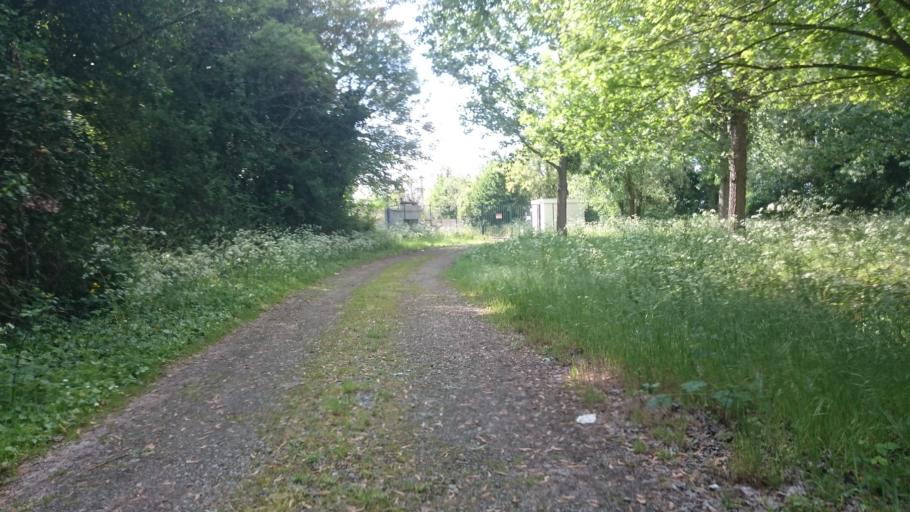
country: FR
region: Pays de la Loire
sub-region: Departement de la Loire-Atlantique
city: La Montagne
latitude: 47.1994
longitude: -1.6913
